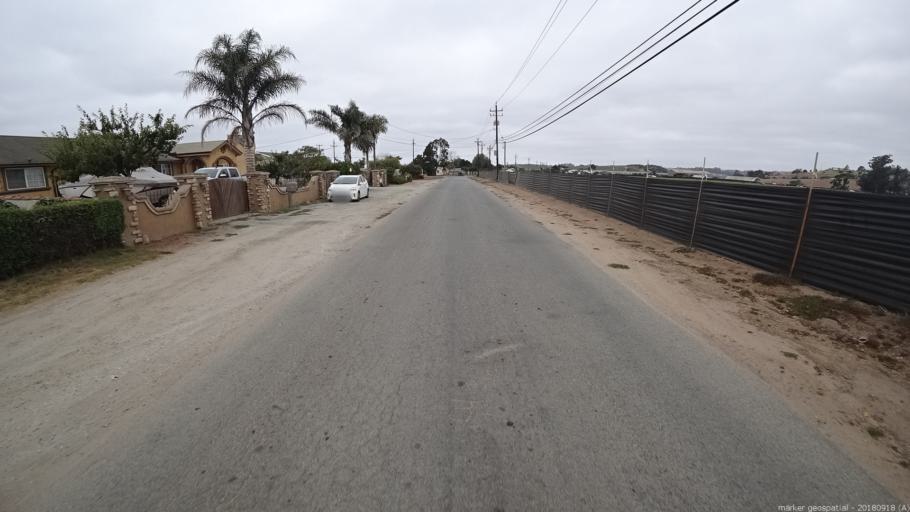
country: US
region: California
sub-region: Monterey County
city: Prunedale
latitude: 36.7498
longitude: -121.6590
